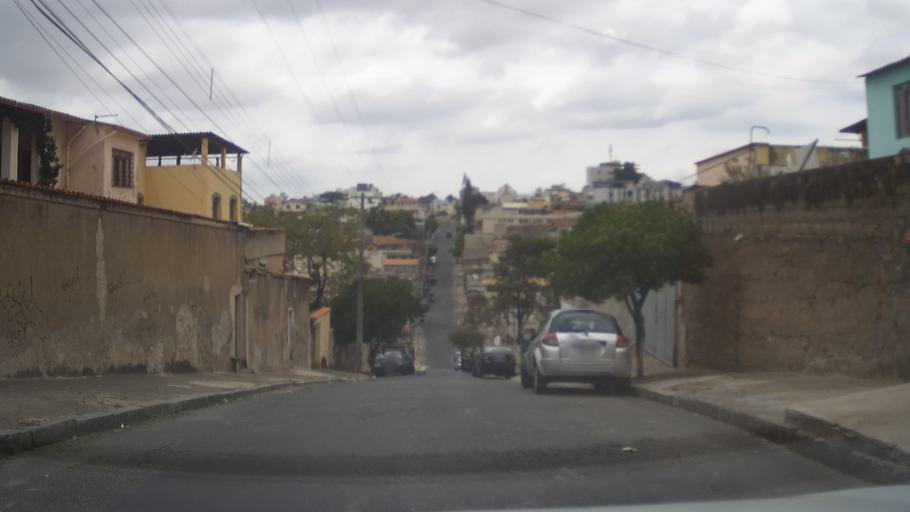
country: BR
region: Minas Gerais
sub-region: Belo Horizonte
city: Belo Horizonte
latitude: -19.9014
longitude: -43.9392
